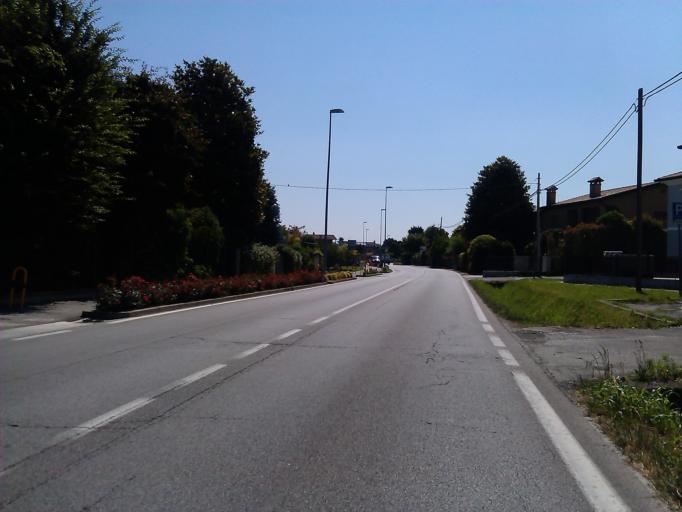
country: IT
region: Veneto
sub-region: Provincia di Treviso
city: Loria Bessica
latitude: 45.7352
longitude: 11.8503
